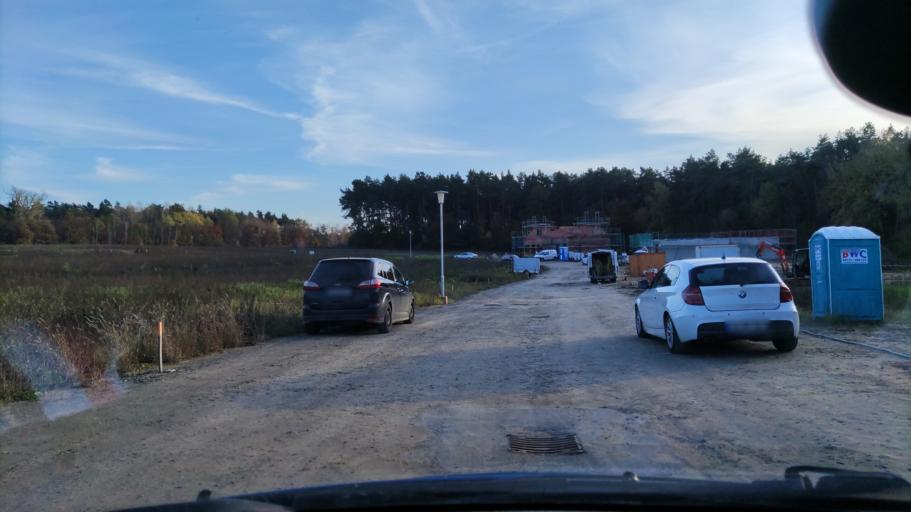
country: DE
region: Lower Saxony
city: Bad Bevensen
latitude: 53.0710
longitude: 10.6004
